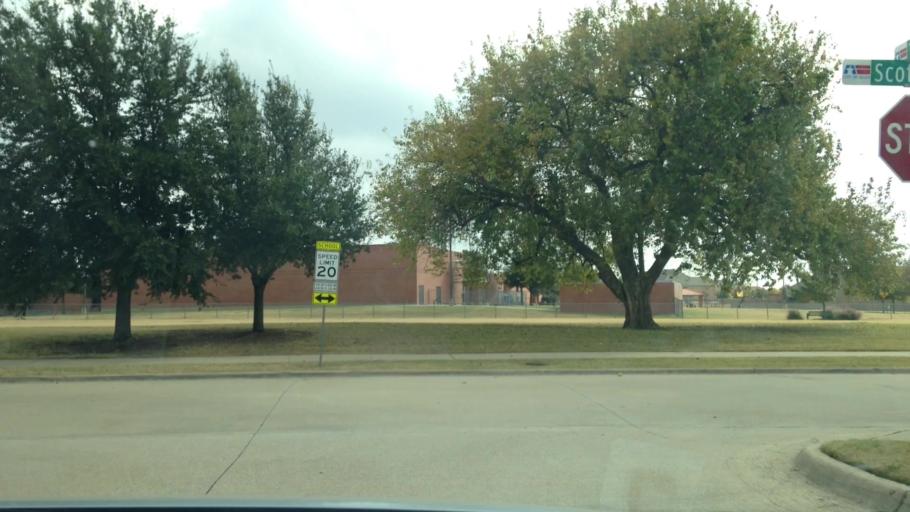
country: US
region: Texas
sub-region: Collin County
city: Allen
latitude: 33.1189
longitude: -96.7040
